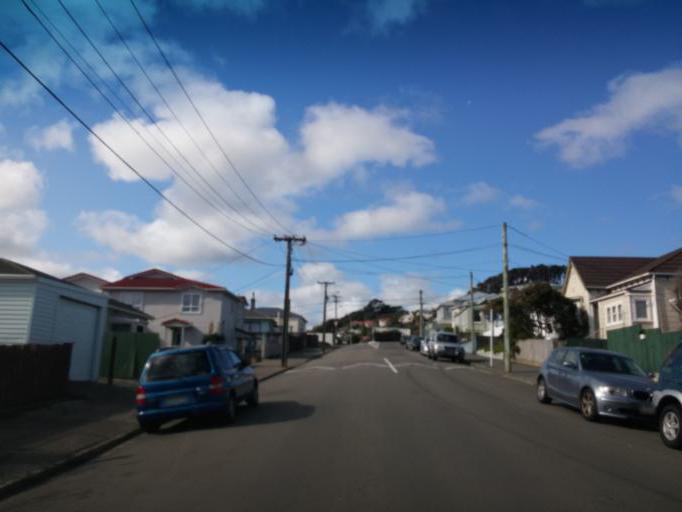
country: NZ
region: Wellington
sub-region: Wellington City
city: Wellington
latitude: -41.3165
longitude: 174.7822
